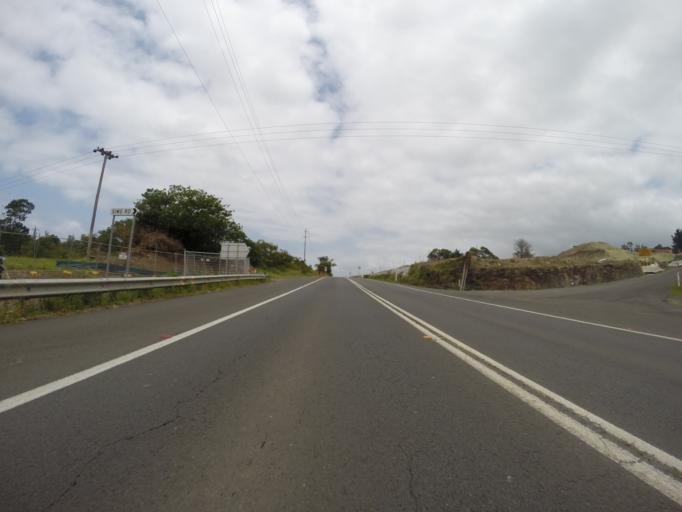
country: AU
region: New South Wales
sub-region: Kiama
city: Gerringong
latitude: -34.7372
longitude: 150.8224
